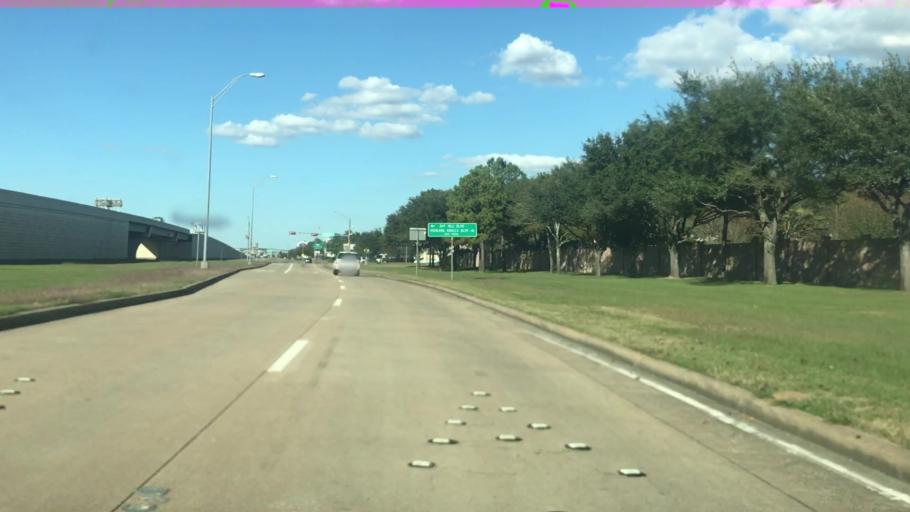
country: US
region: Texas
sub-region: Fort Bend County
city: Cinco Ranch
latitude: 29.7550
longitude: -95.7757
